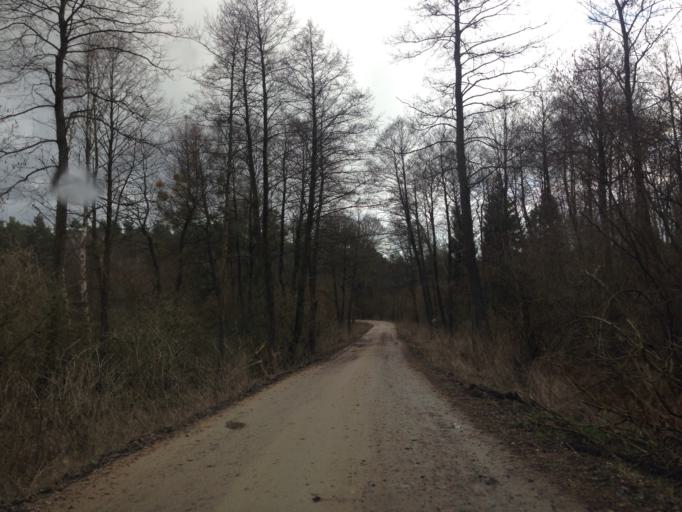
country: PL
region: Kujawsko-Pomorskie
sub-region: Powiat brodnicki
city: Gorzno
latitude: 53.2278
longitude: 19.6625
